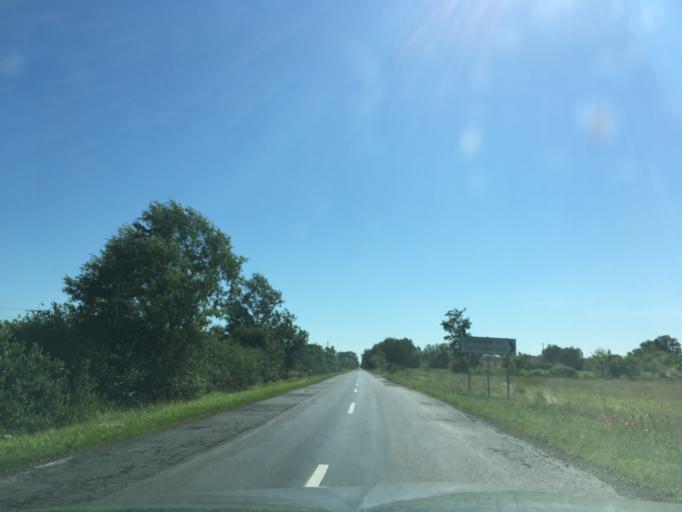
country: HU
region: Hajdu-Bihar
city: Hajdusamson
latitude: 47.5247
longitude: 21.7609
